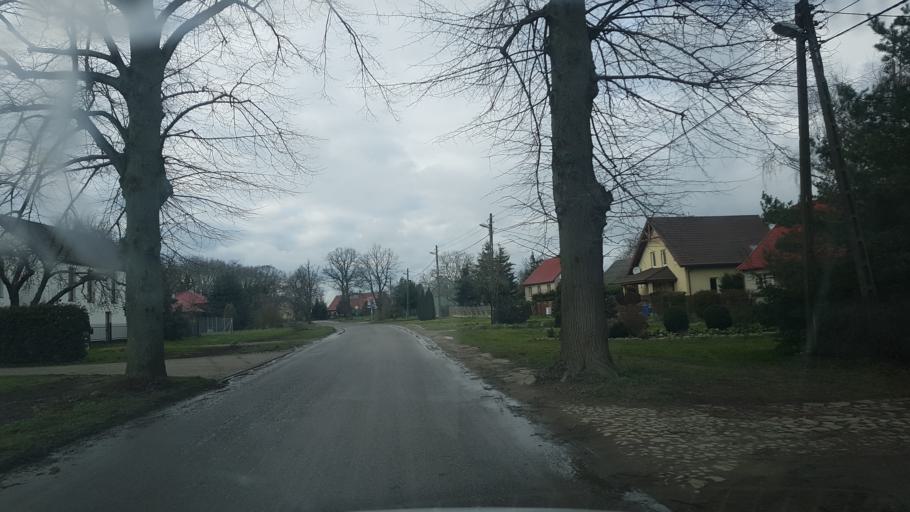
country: PL
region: West Pomeranian Voivodeship
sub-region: Powiat policki
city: Kolbaskowo
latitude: 53.3564
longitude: 14.4413
